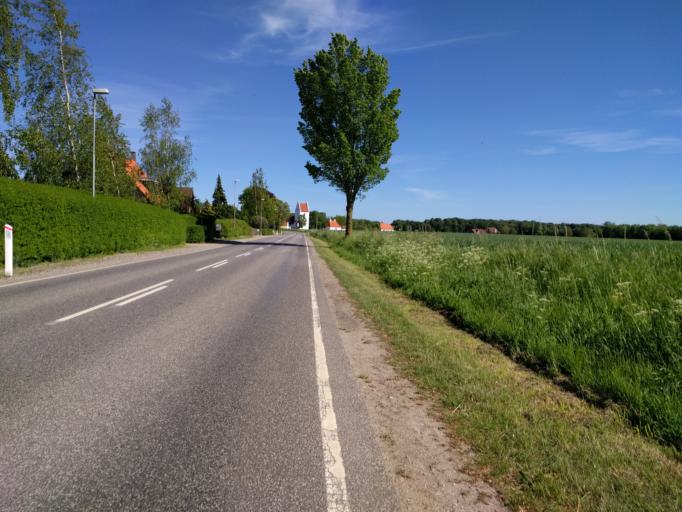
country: DK
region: South Denmark
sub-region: Kerteminde Kommune
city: Kerteminde
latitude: 55.4182
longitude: 10.6566
